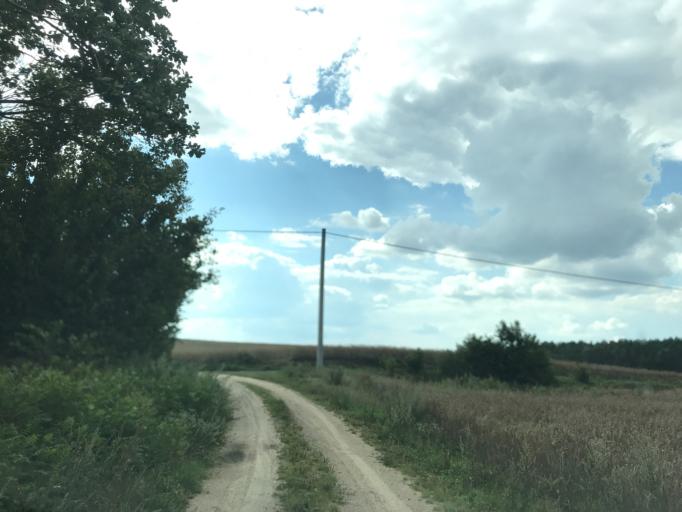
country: PL
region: Kujawsko-Pomorskie
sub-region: Powiat brodnicki
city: Brzozie
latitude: 53.3151
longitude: 19.6827
